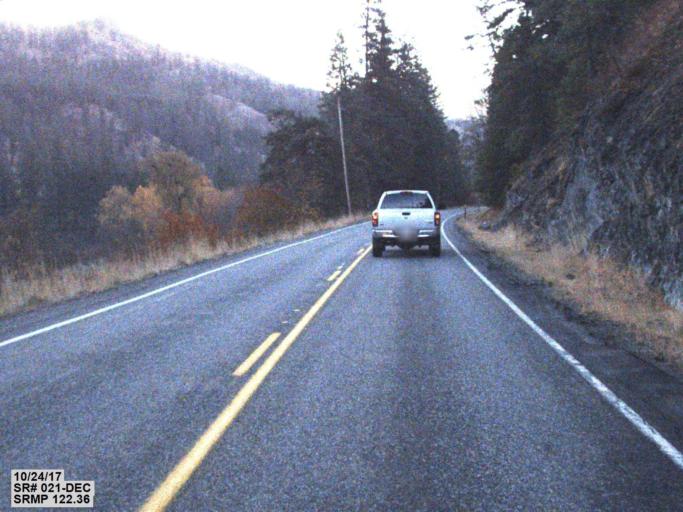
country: US
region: Washington
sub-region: Okanogan County
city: Coulee Dam
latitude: 48.1544
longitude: -118.6991
